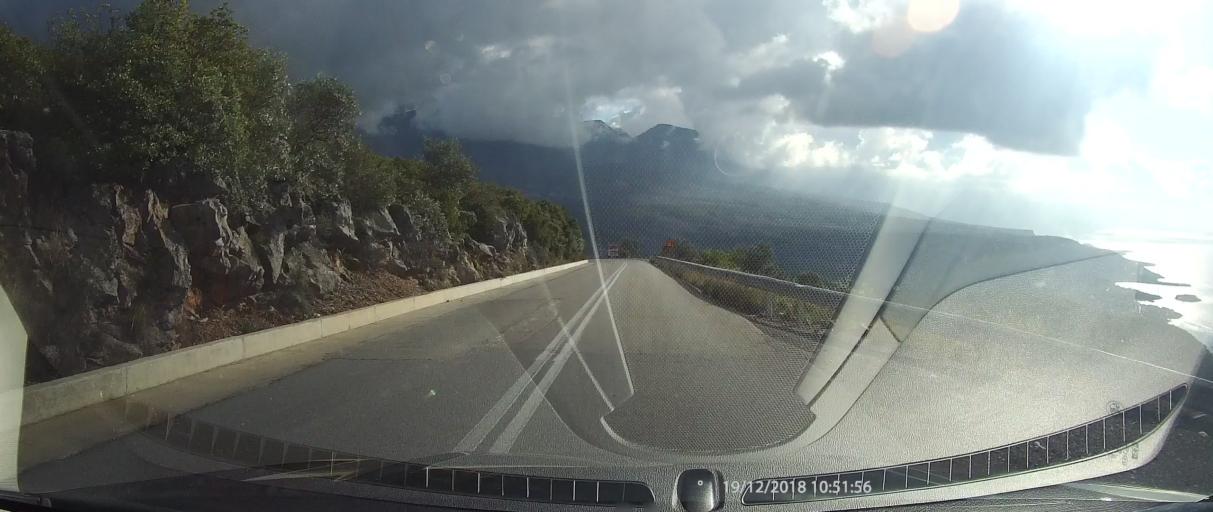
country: GR
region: Peloponnese
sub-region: Nomos Messinias
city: Kardamyli
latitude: 36.9128
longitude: 22.2200
